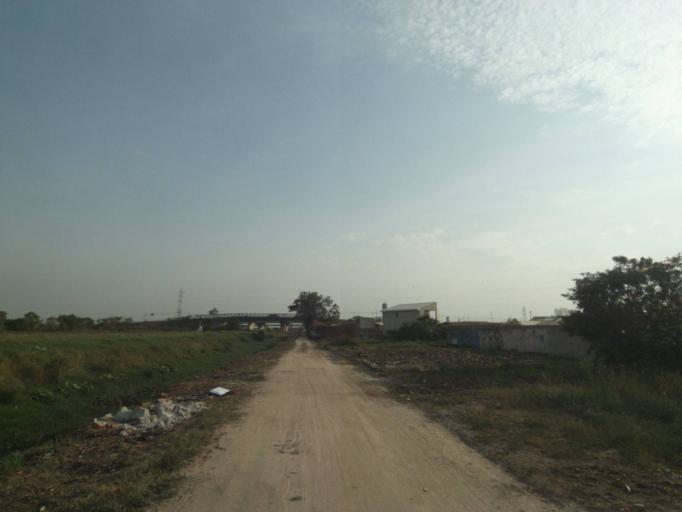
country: BR
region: Parana
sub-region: Sao Jose Dos Pinhais
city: Sao Jose dos Pinhais
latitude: -25.4990
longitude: -49.2073
